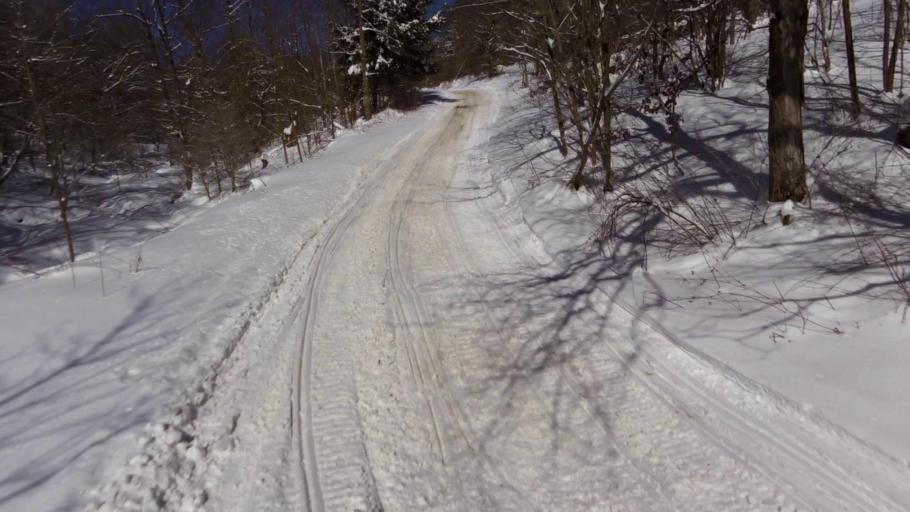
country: US
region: New York
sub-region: Chautauqua County
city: Mayville
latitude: 42.2550
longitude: -79.4413
